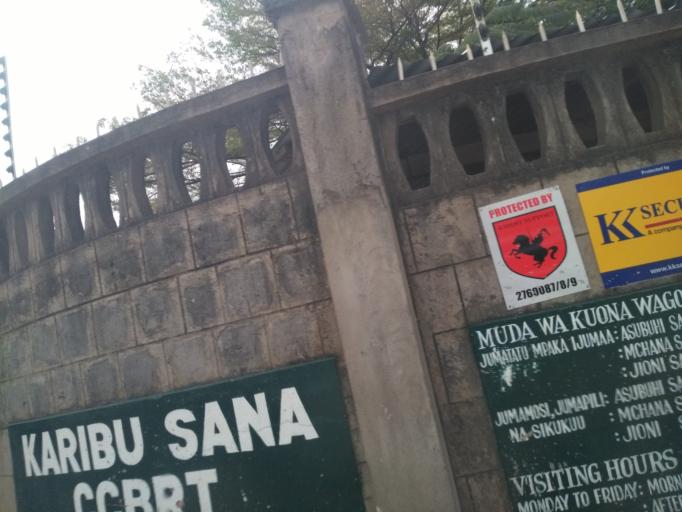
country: TZ
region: Dar es Salaam
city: Magomeni
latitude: -6.7685
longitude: 39.2714
